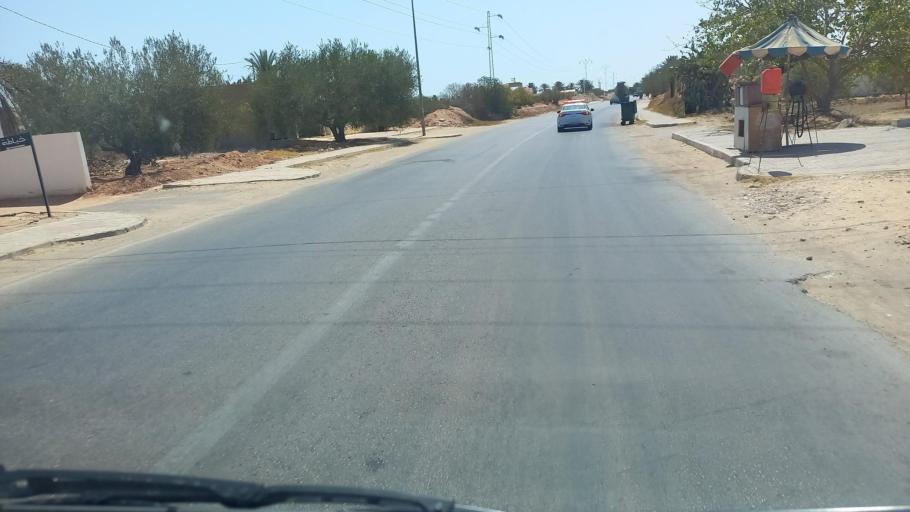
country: TN
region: Madanin
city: Midoun
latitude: 33.7736
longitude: 10.8968
